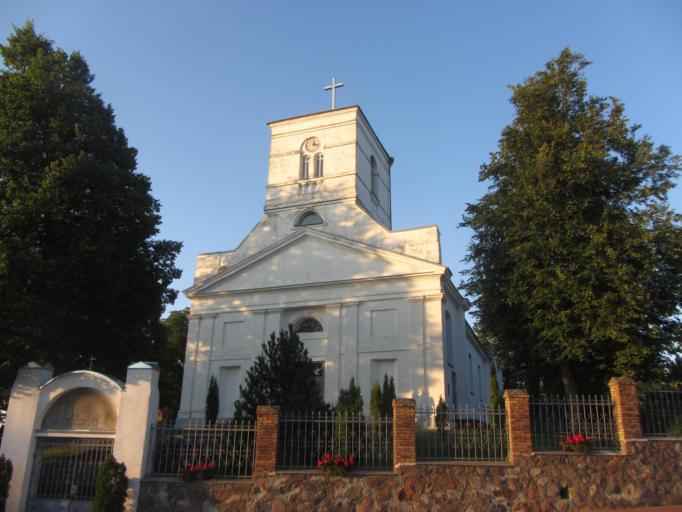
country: LT
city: Veisiejai
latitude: 54.2306
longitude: 23.8151
